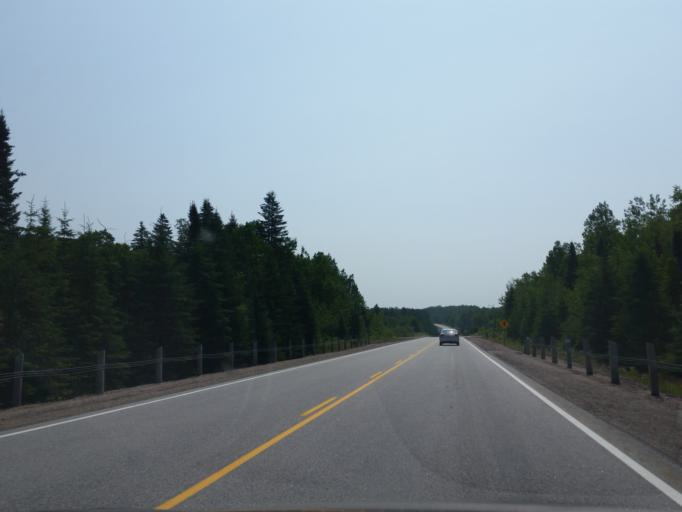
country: CA
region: Ontario
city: Mattawa
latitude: 46.2816
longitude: -78.4992
